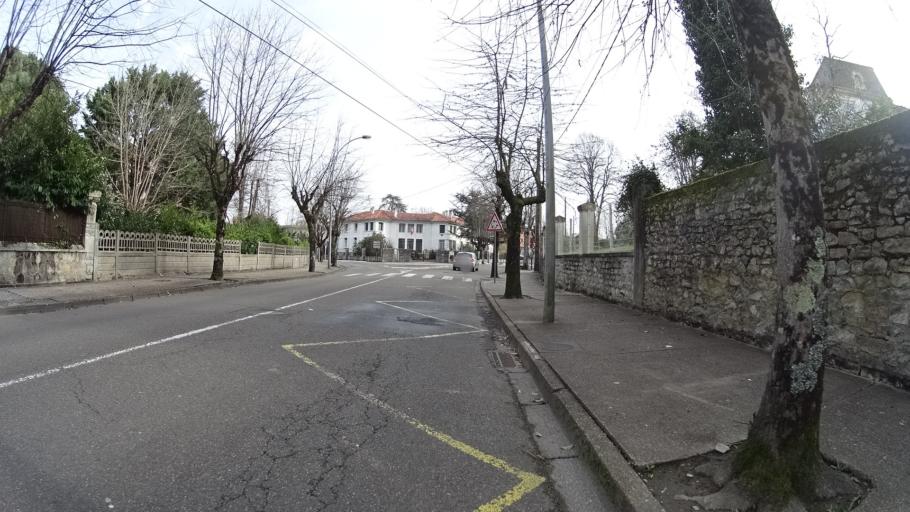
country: FR
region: Aquitaine
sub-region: Departement des Landes
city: Dax
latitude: 43.7042
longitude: -1.0572
